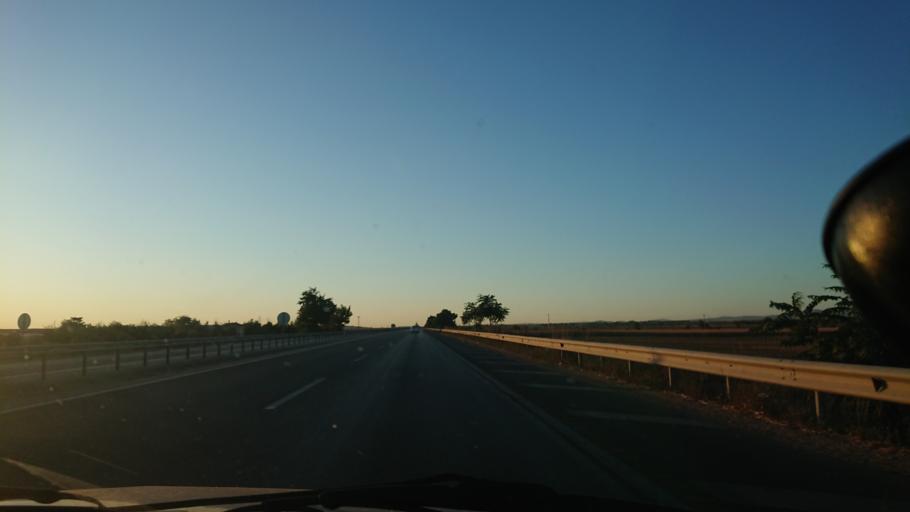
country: TR
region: Eskisehir
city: Mahmudiye
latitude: 39.5403
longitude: 30.9400
